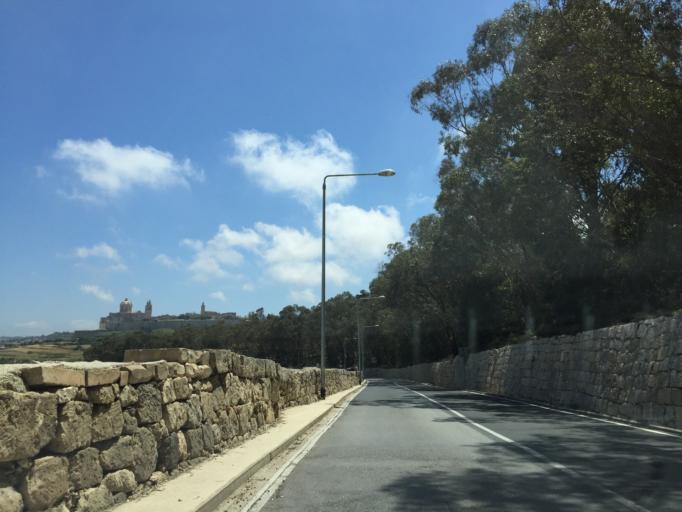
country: MT
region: L-Imtarfa
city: Imtarfa
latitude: 35.8948
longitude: 14.4034
